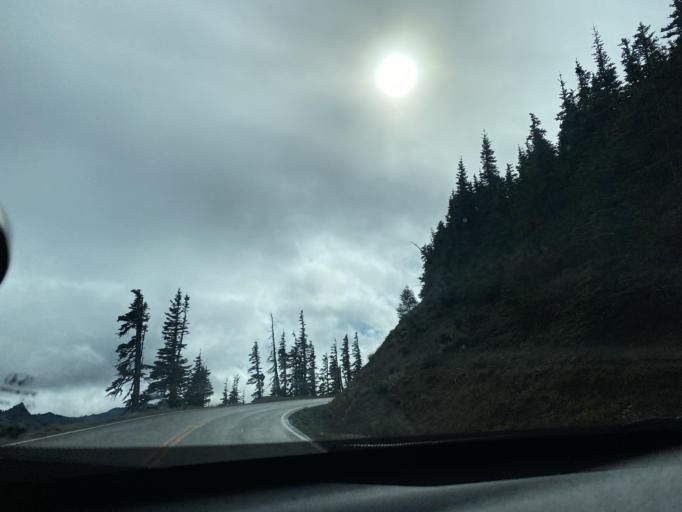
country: US
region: Washington
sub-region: Clallam County
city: Port Angeles
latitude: 47.9702
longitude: -123.4865
